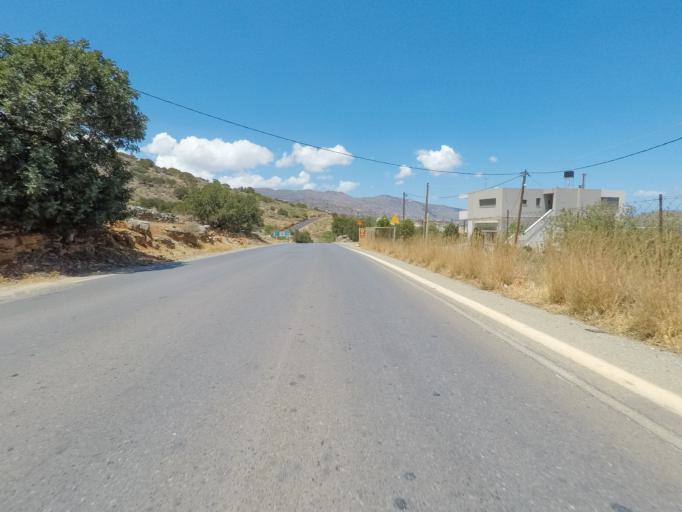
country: GR
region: Crete
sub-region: Nomos Lasithiou
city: Skhisma
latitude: 35.2471
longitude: 25.7246
